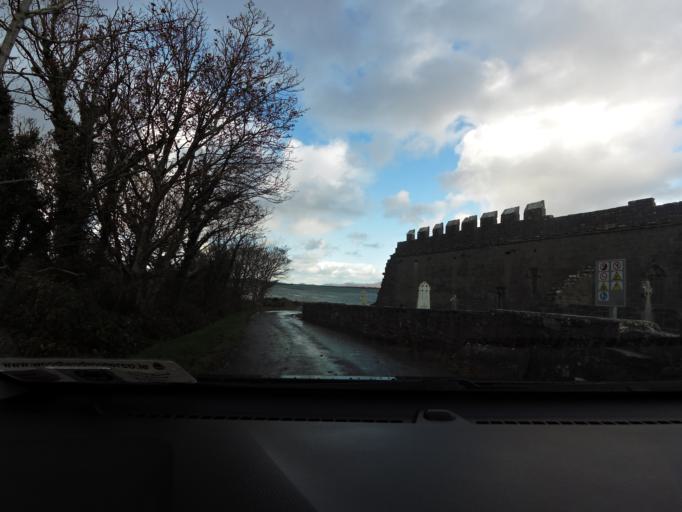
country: IE
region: Connaught
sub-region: Maigh Eo
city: Westport
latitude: 53.7818
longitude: -9.6395
